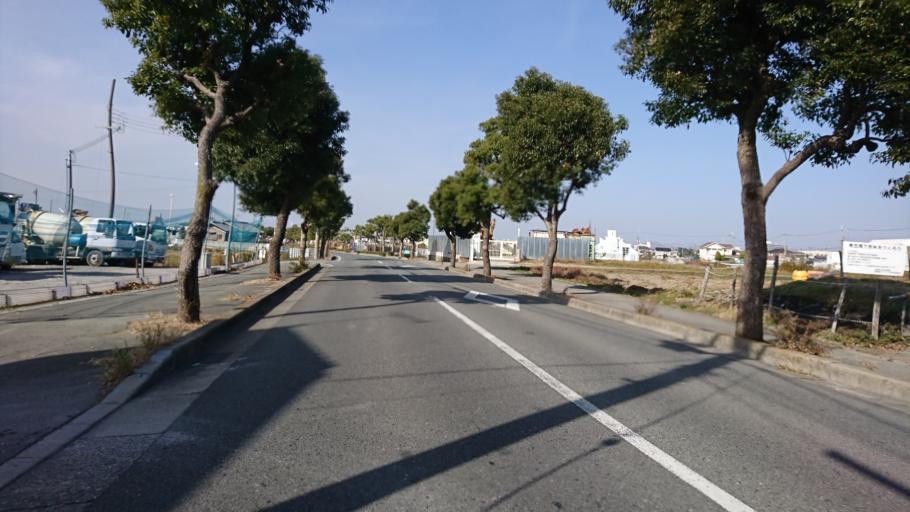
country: JP
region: Hyogo
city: Kakogawacho-honmachi
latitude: 34.7275
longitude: 134.8755
